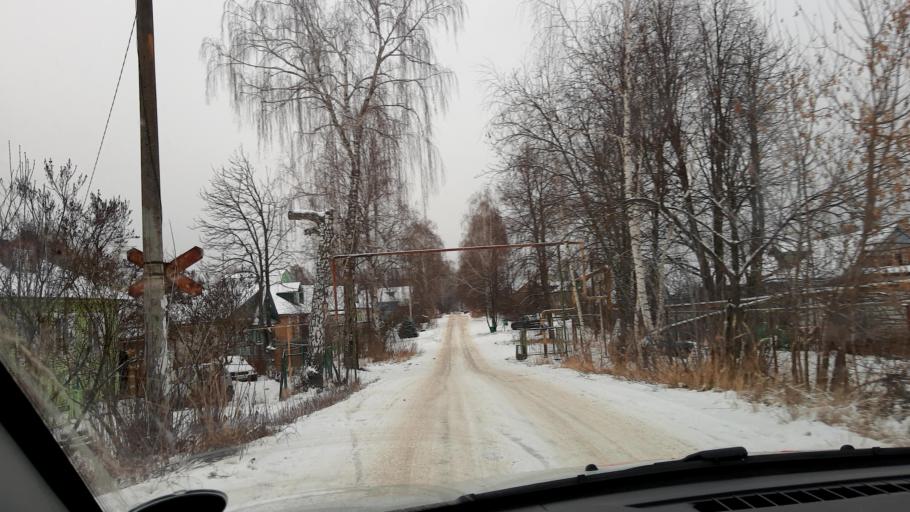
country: RU
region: Nizjnij Novgorod
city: Burevestnik
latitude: 56.1970
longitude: 43.7720
